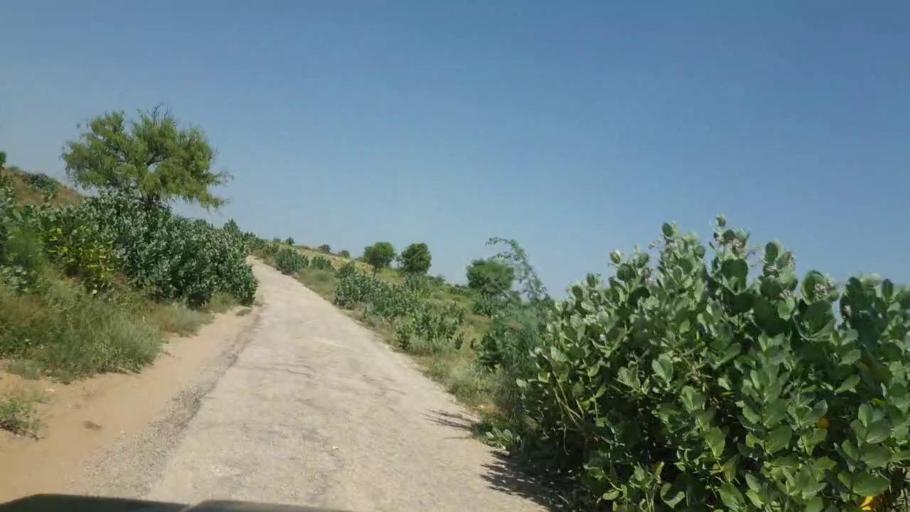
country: PK
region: Sindh
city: Chor
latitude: 25.3954
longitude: 70.3135
